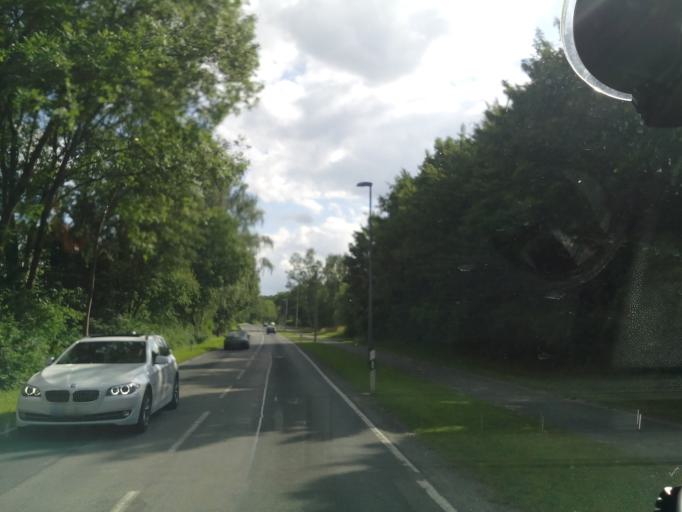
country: DE
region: Bavaria
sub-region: Upper Franconia
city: Neustadt bei Coburg
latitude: 50.3237
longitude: 11.1082
